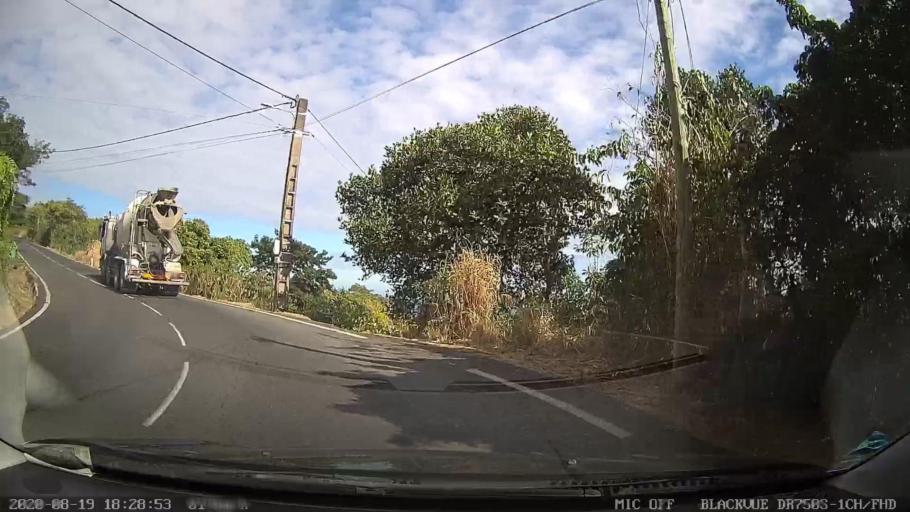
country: RE
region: Reunion
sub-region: Reunion
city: La Possession
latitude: -20.9568
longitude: 55.3507
